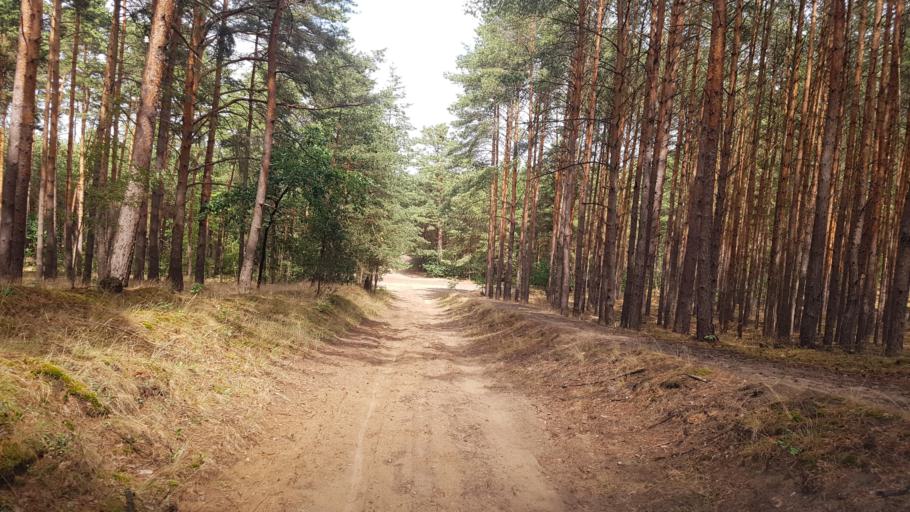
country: DE
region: Brandenburg
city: Trebbin
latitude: 52.2505
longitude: 13.1839
